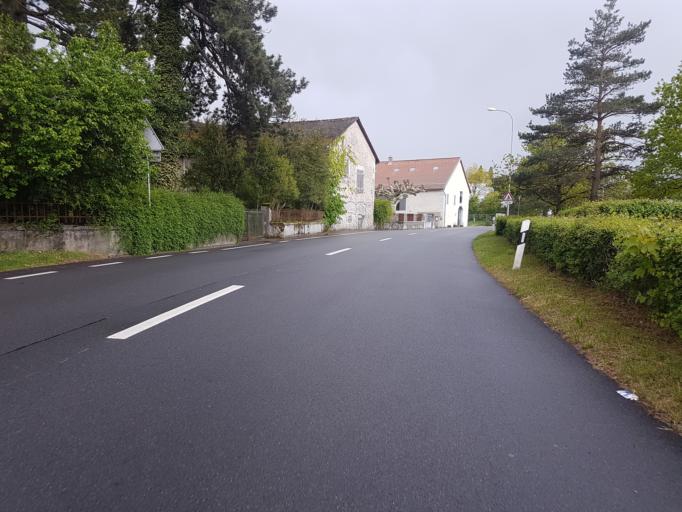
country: CH
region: Geneva
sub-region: Geneva
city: Dardagny
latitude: 46.1787
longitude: 6.0066
